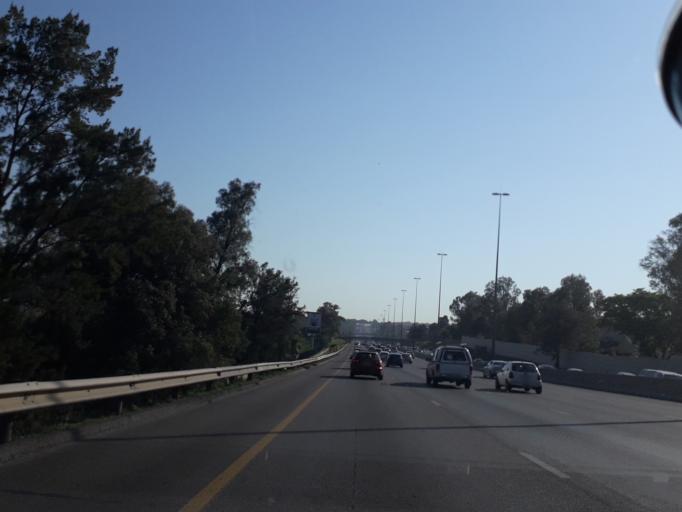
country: ZA
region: Gauteng
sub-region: City of Johannesburg Metropolitan Municipality
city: Diepsloot
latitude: -26.0573
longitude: 27.9881
